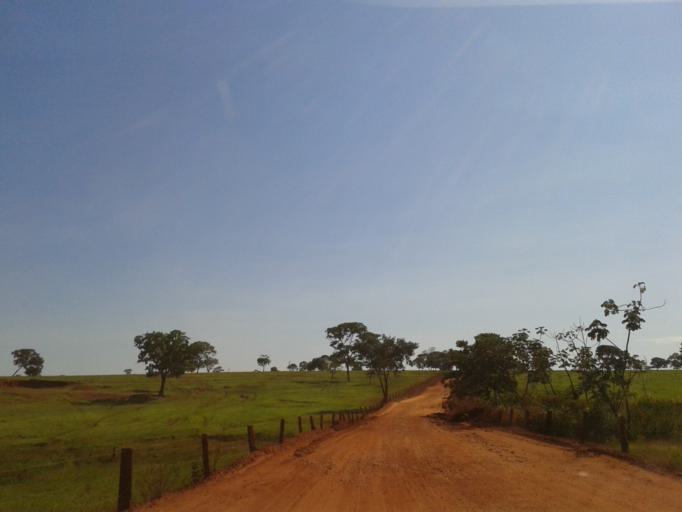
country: BR
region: Minas Gerais
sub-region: Santa Vitoria
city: Santa Vitoria
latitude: -19.1016
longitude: -50.5064
